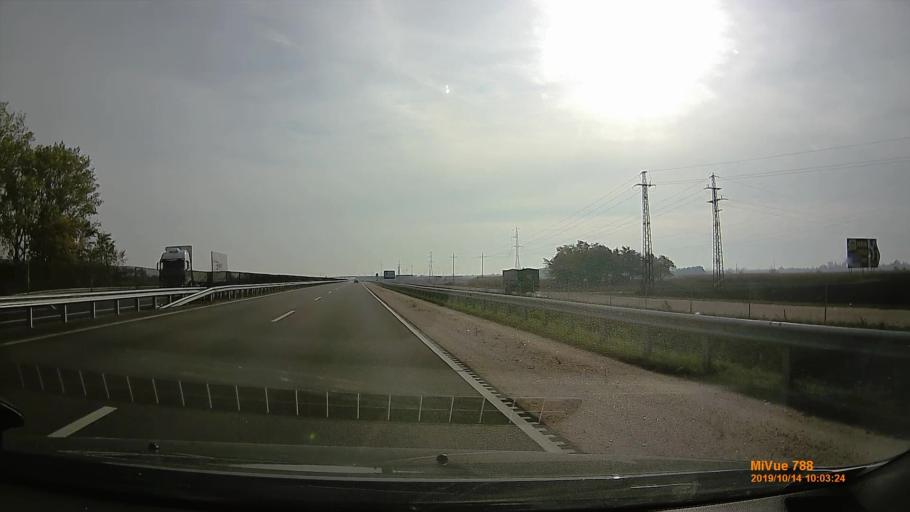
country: HU
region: Pest
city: Cegled
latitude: 47.2059
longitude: 19.7677
